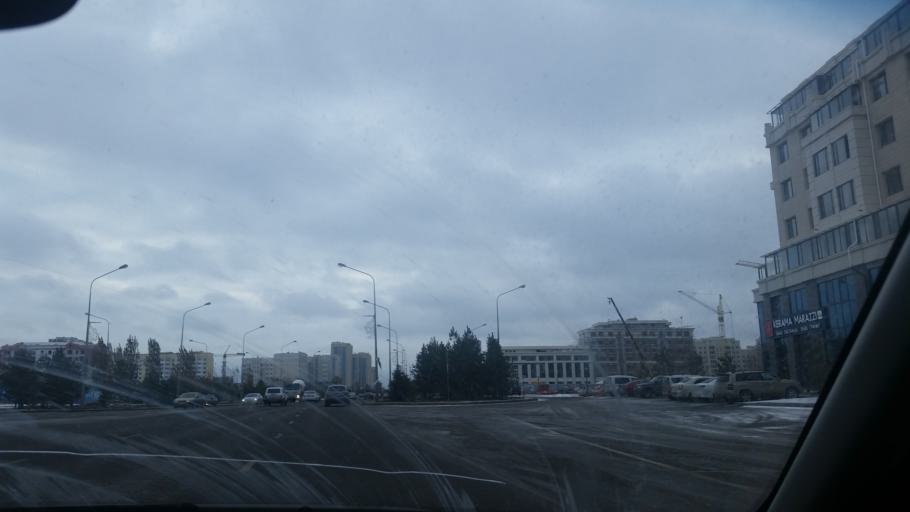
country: KZ
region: Astana Qalasy
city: Astana
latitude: 51.1031
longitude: 71.4294
